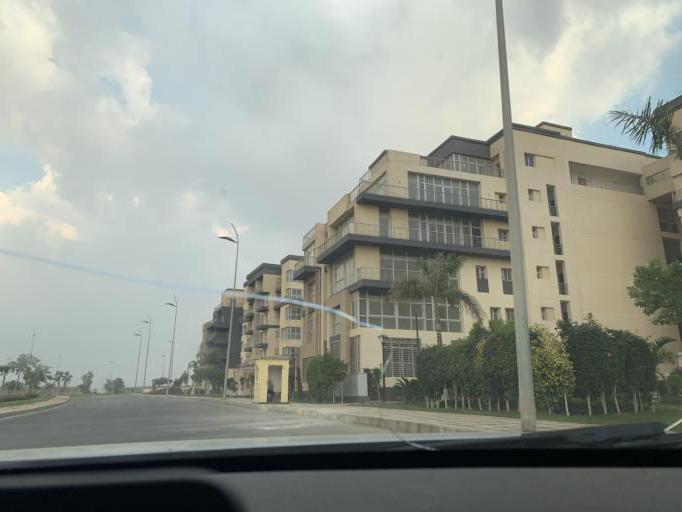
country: EG
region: Muhafazat al Qalyubiyah
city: Al Khankah
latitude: 30.1040
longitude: 31.6552
